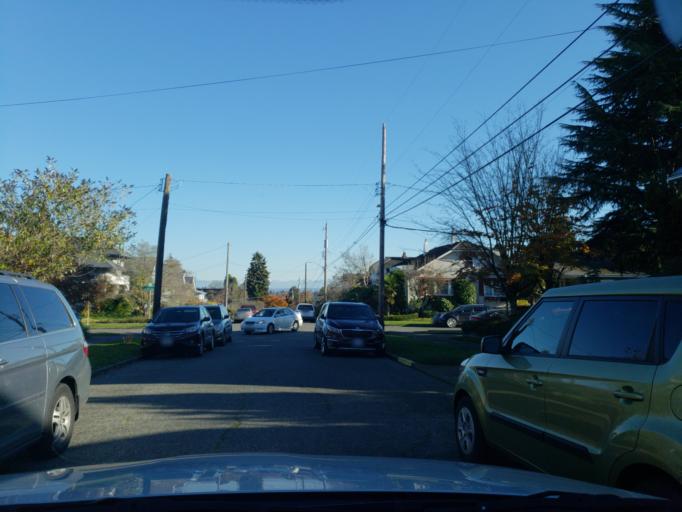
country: US
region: Washington
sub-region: King County
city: Seattle
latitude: 47.6725
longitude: -122.3534
